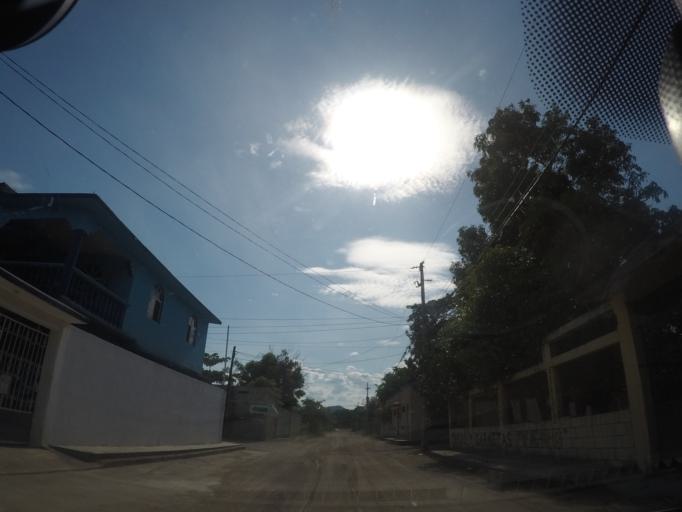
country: MX
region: Oaxaca
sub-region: Salina Cruz
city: Salina Cruz
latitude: 16.2163
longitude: -95.1985
